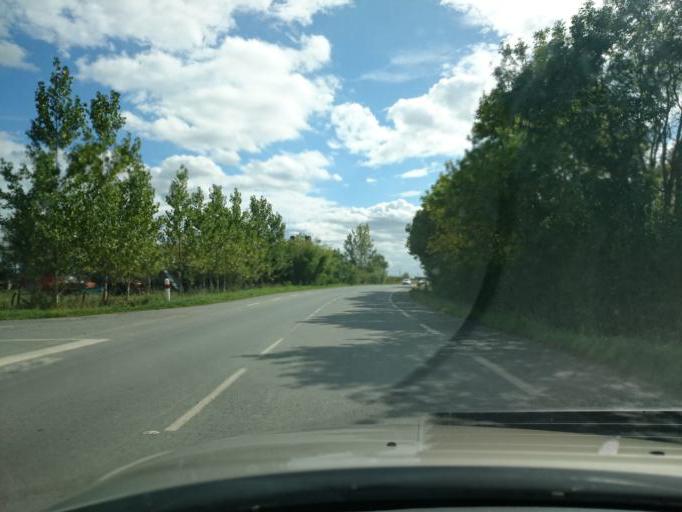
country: FR
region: Aquitaine
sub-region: Departement de la Gironde
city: Saint-Louis-de-Montferrand
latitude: 44.9274
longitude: -0.5622
